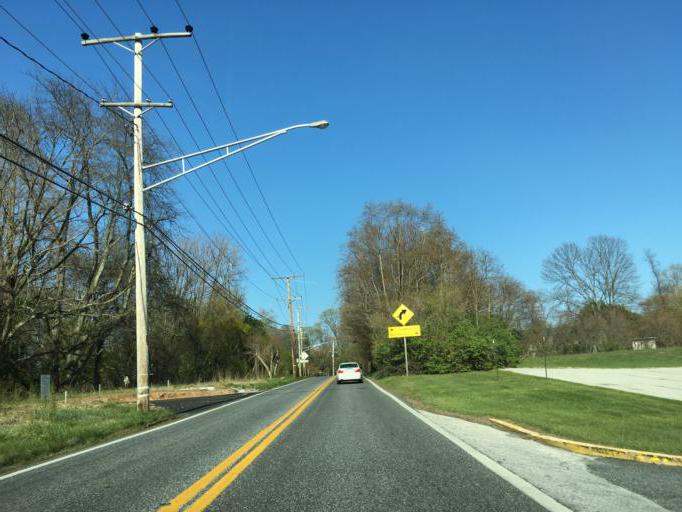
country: US
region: Maryland
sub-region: Baltimore County
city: Hunt Valley
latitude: 39.5132
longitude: -76.5493
